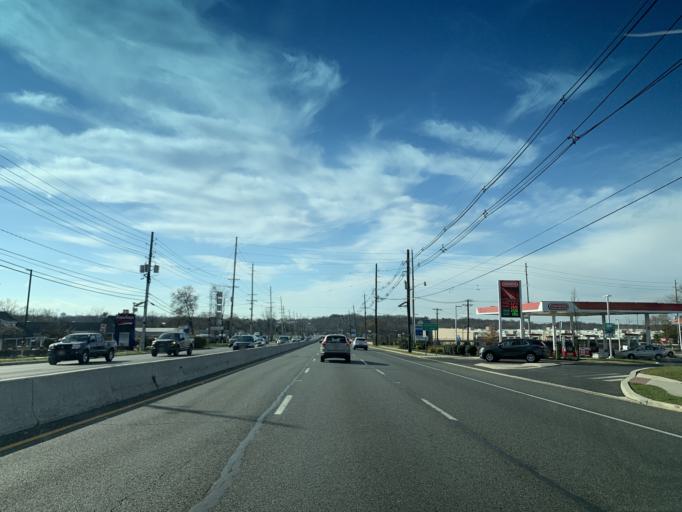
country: US
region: New Jersey
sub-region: Burlington County
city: Cinnaminson
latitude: 40.0070
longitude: -74.9738
